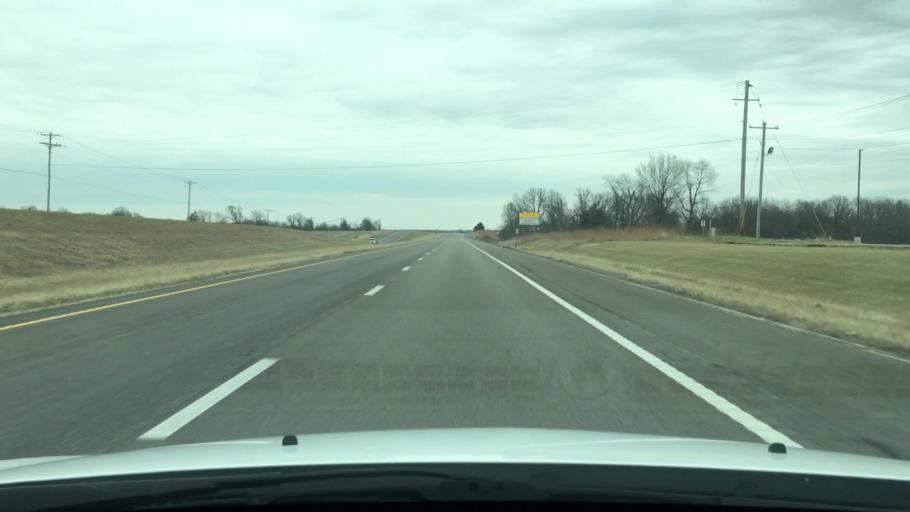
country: US
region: Missouri
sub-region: Callaway County
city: Fulton
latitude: 38.9615
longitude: -91.9188
